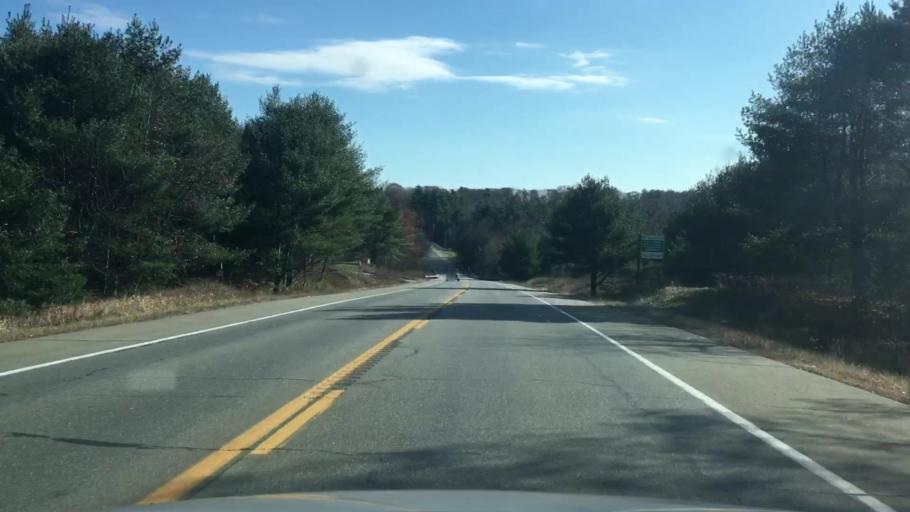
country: US
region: Maine
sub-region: Kennebec County
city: Windsor
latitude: 44.2597
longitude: -69.5558
